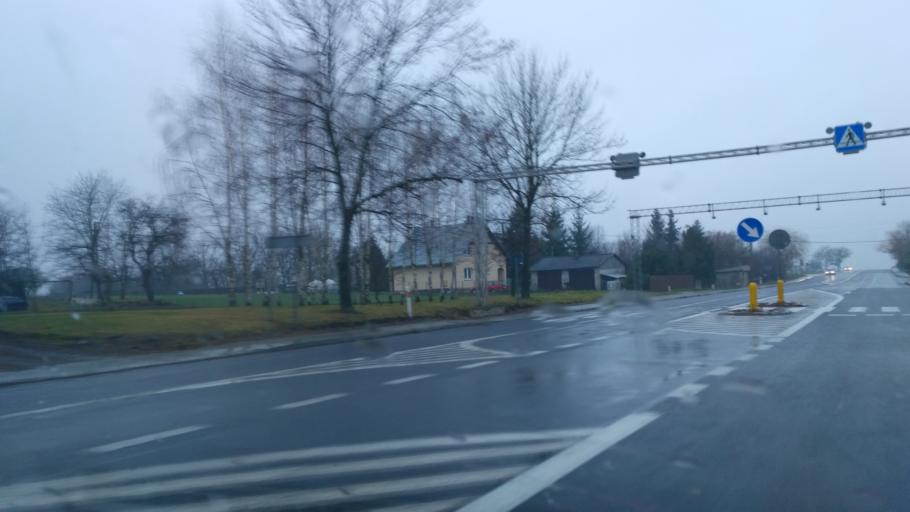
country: PL
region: Subcarpathian Voivodeship
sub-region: Powiat lancucki
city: Rogozno
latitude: 50.0682
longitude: 22.3753
